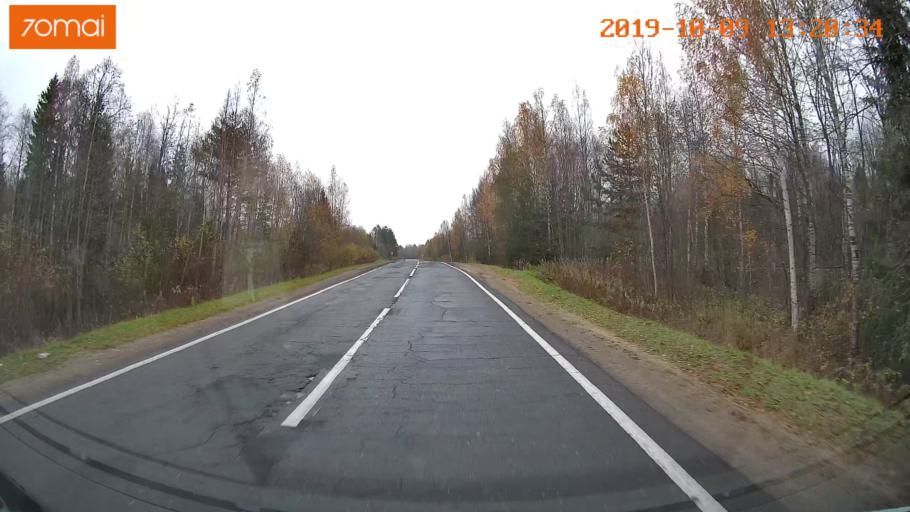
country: RU
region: Jaroslavl
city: Lyubim
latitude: 58.3424
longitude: 40.8313
